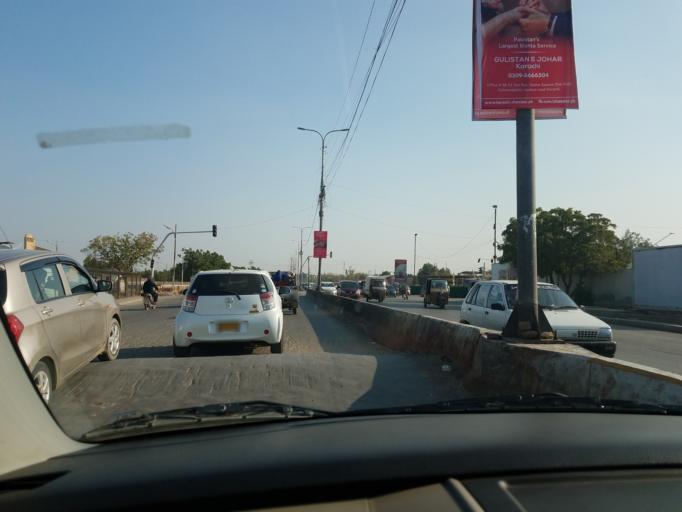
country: PK
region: Sindh
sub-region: Karachi District
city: Karachi
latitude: 24.8927
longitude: 67.1214
